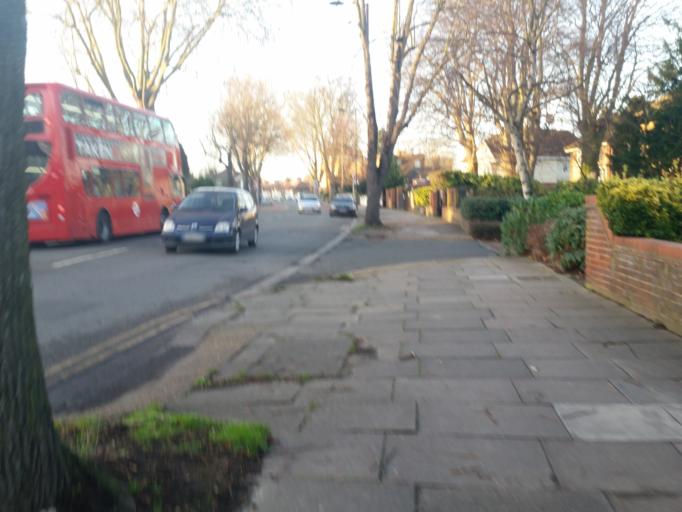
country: GB
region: England
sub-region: Greater London
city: Enfield
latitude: 51.6436
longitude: -0.0802
